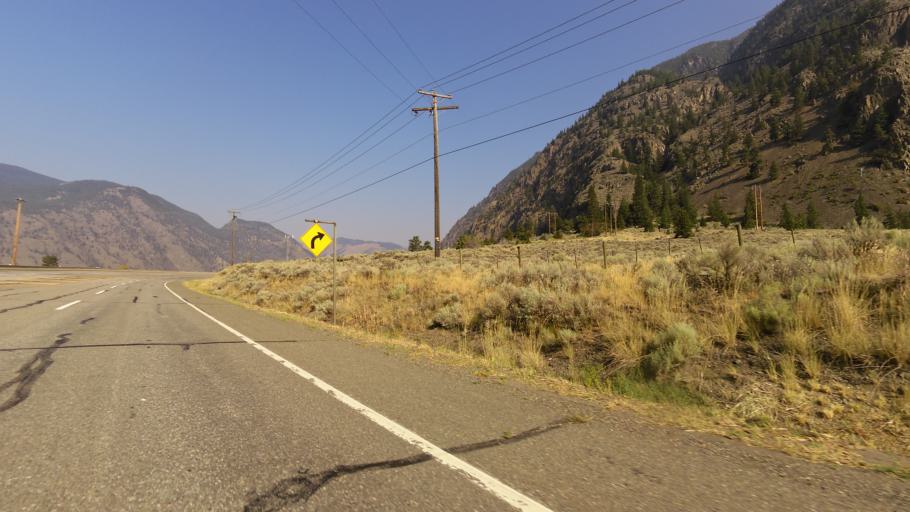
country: CA
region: British Columbia
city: Oliver
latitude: 49.2206
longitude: -119.9527
